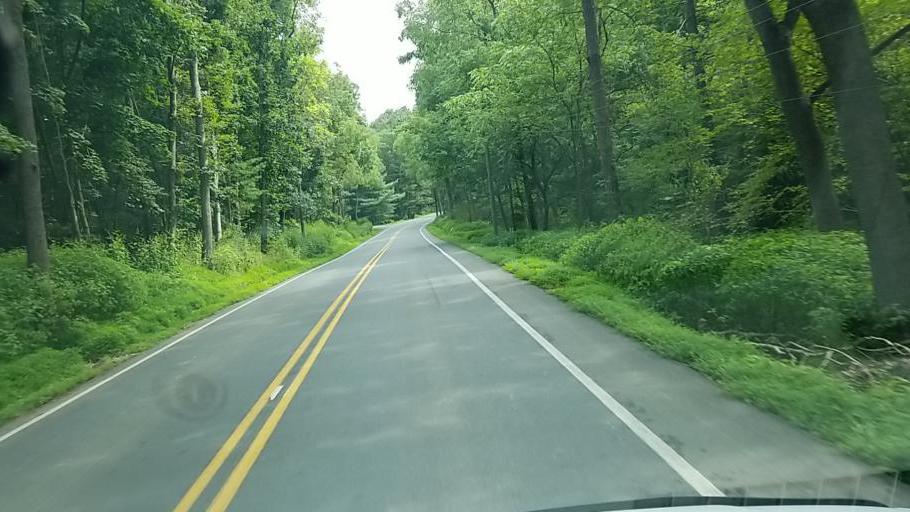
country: US
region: Pennsylvania
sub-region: Dauphin County
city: Elizabethville
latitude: 40.6224
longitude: -76.7854
